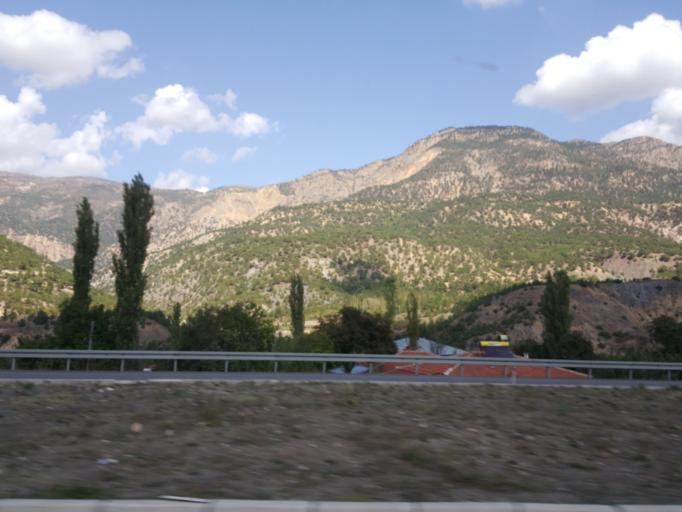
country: TR
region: Sivas
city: Dogansar
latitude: 40.3118
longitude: 37.6474
